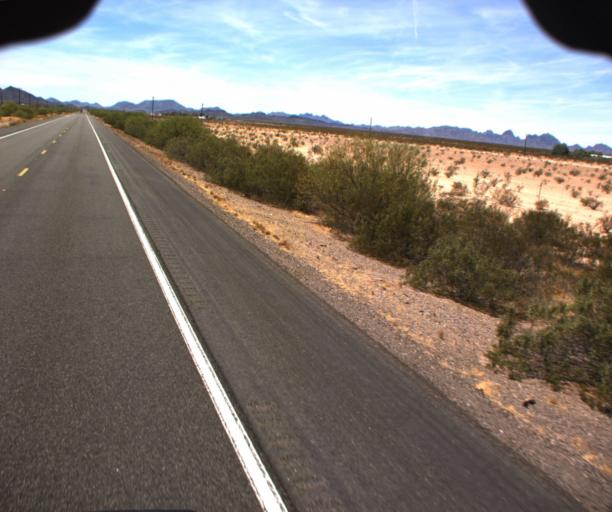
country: US
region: Arizona
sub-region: La Paz County
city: Salome
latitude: 33.7016
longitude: -113.8505
